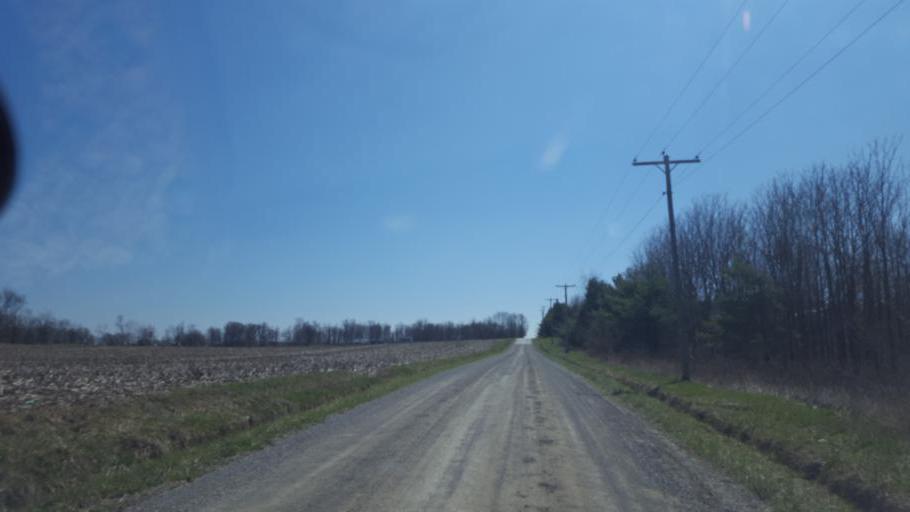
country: US
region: Ohio
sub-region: Ashland County
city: Ashland
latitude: 40.9084
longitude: -82.3587
